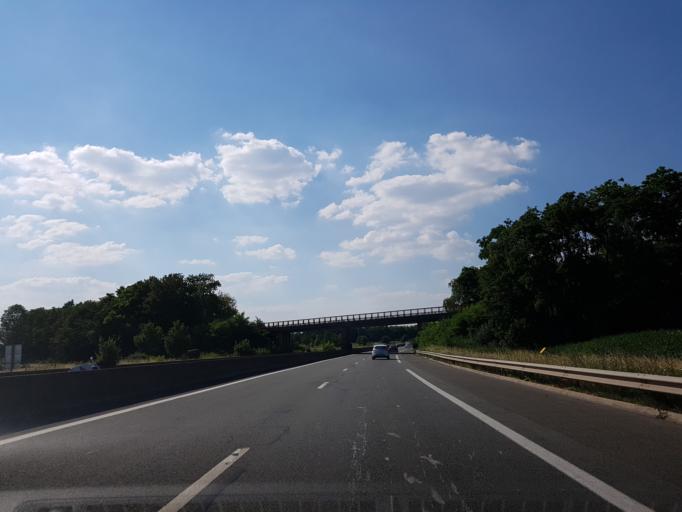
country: FR
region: Nord-Pas-de-Calais
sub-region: Departement du Nord
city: Escaudain
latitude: 50.3330
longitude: 3.3249
